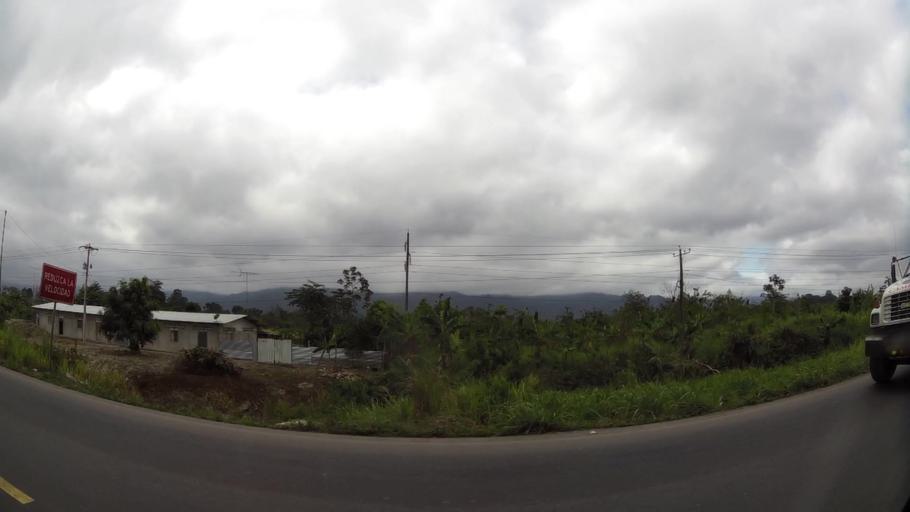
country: EC
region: Guayas
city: Naranjal
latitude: -2.6871
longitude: -79.6345
